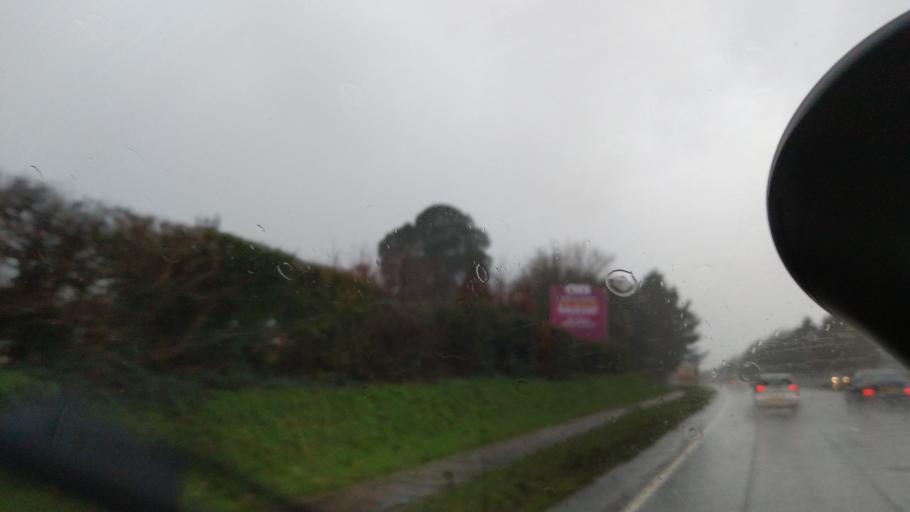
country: GB
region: England
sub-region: West Sussex
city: Fontwell
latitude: 50.8564
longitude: -0.6556
